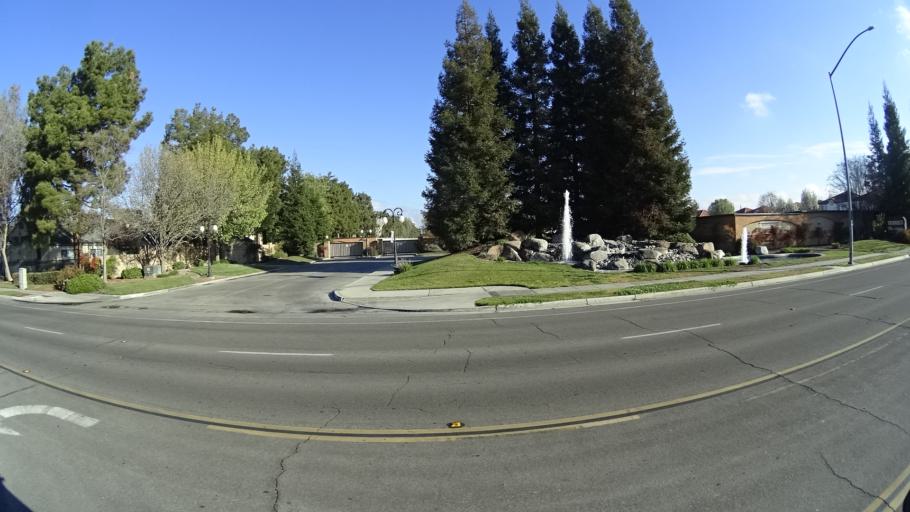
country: US
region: California
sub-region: Fresno County
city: West Park
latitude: 36.8118
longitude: -119.8568
